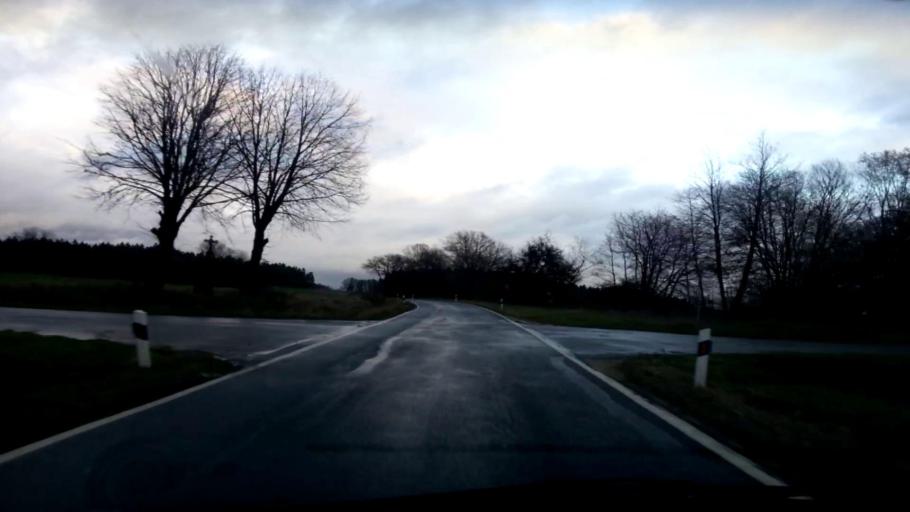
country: DE
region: Bavaria
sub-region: Upper Franconia
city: Konigsfeld
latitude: 49.9255
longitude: 11.1555
